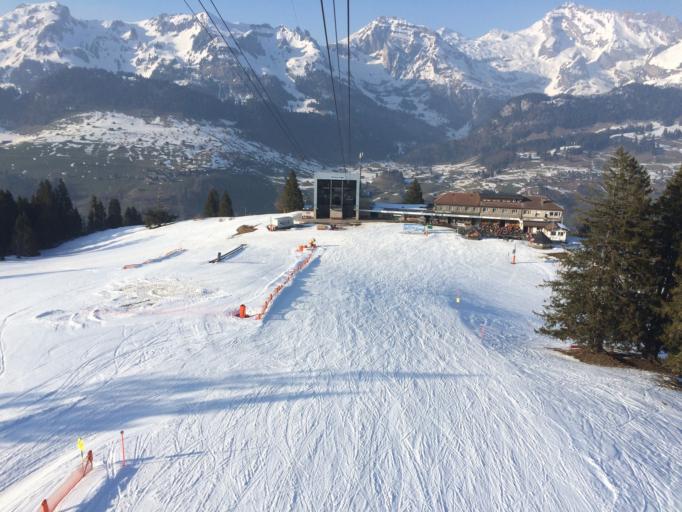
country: CH
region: Saint Gallen
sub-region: Wahlkreis Toggenburg
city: Wildhaus
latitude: 47.1836
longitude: 9.3119
